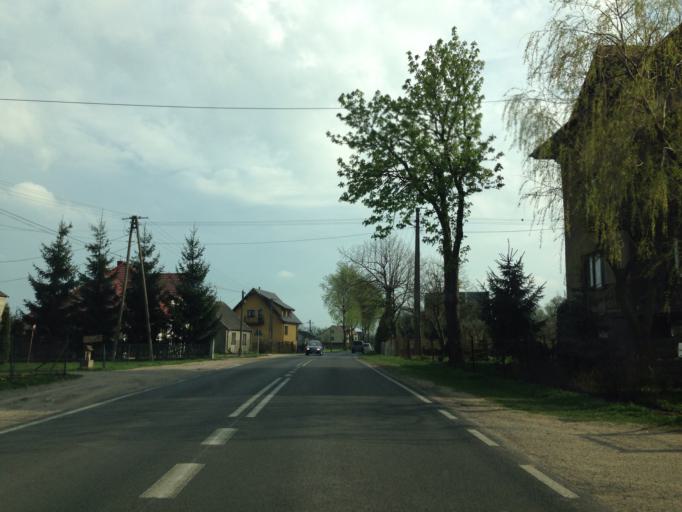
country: PL
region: Masovian Voivodeship
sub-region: Powiat zurominski
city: Zuromin
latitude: 53.0413
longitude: 19.9150
